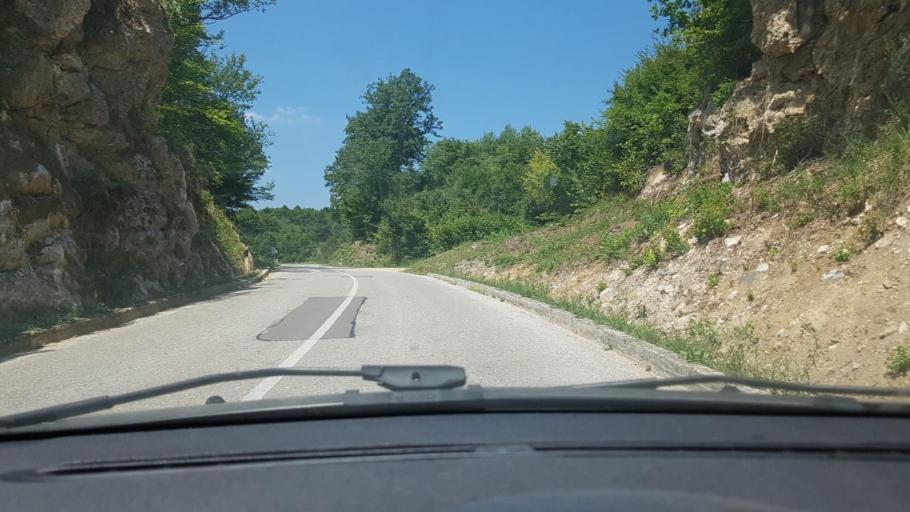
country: BA
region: Federation of Bosnia and Herzegovina
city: Orasac
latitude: 44.5966
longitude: 16.0758
